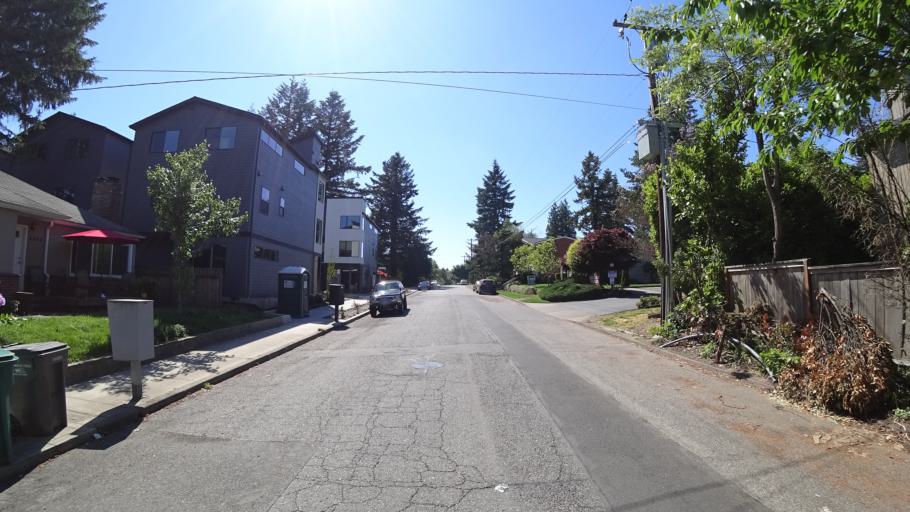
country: US
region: Oregon
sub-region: Washington County
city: Metzger
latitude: 45.4507
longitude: -122.7243
